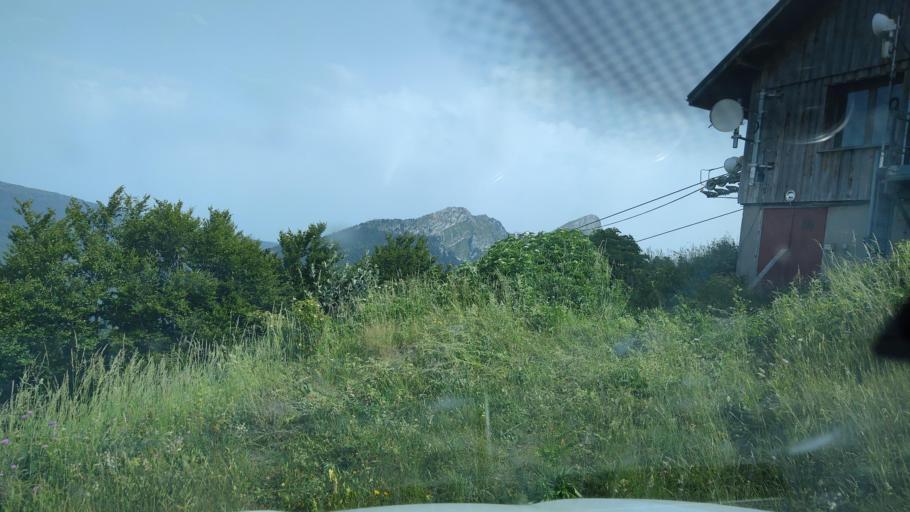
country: FR
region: Rhone-Alpes
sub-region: Departement de la Savoie
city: Cruet
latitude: 45.5940
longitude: 6.1135
